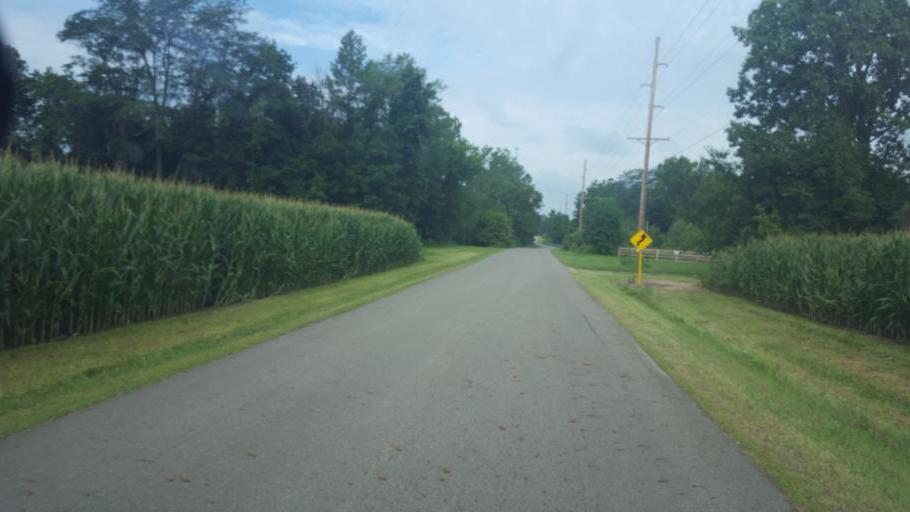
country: US
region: Ohio
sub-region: Delaware County
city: Ashley
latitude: 40.3609
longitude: -82.8919
